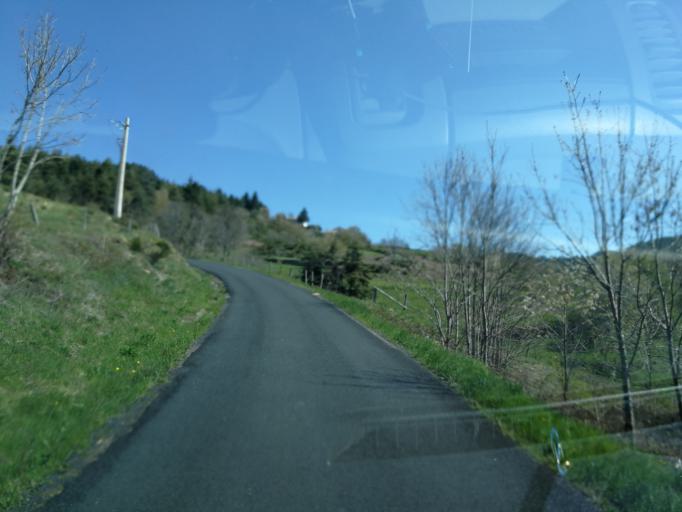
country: FR
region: Rhone-Alpes
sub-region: Departement de l'Ardeche
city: Le Cheylard
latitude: 44.9364
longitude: 4.4246
